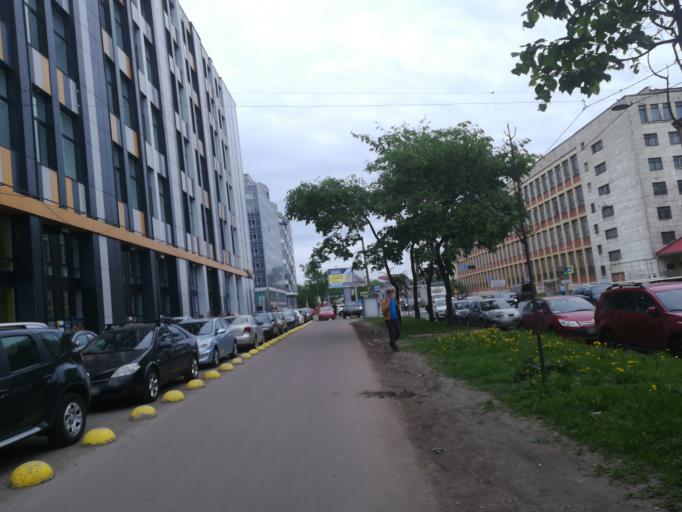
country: RU
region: St.-Petersburg
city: Vasyl'evsky Ostrov
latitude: 59.9502
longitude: 30.2669
